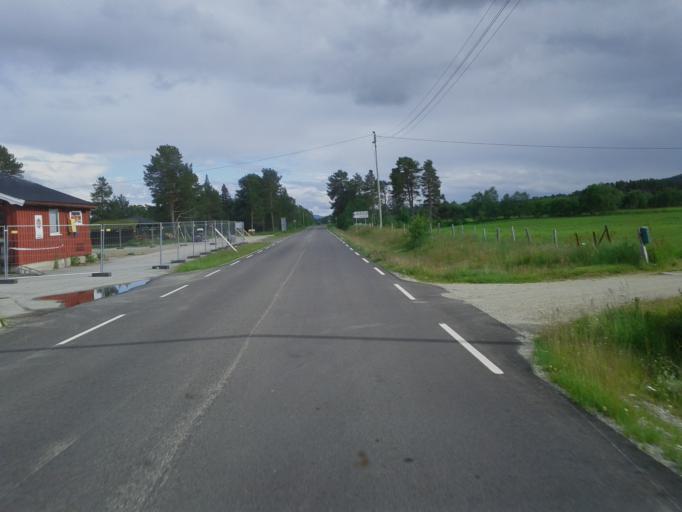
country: NO
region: Sor-Trondelag
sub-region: Roros
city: Roros
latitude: 62.2867
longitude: 11.7346
